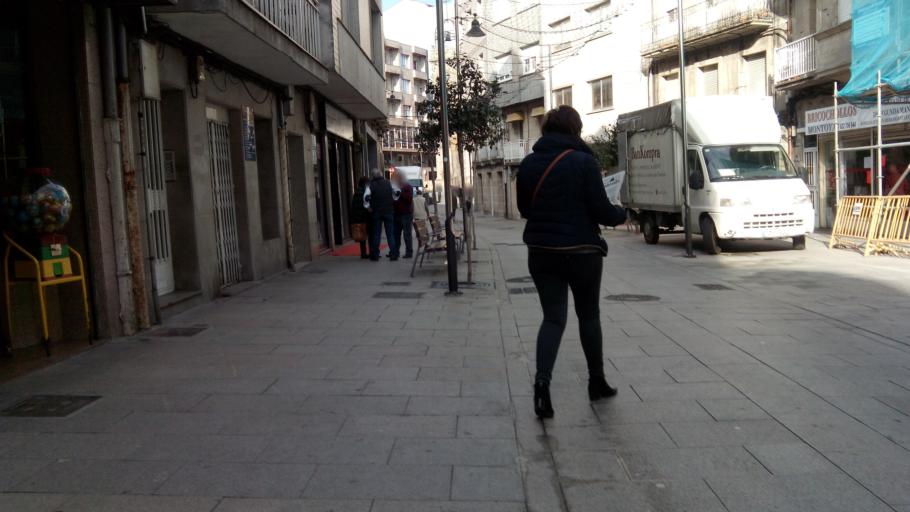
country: ES
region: Galicia
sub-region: Provincia de Pontevedra
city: Marin
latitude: 42.3917
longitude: -8.7030
